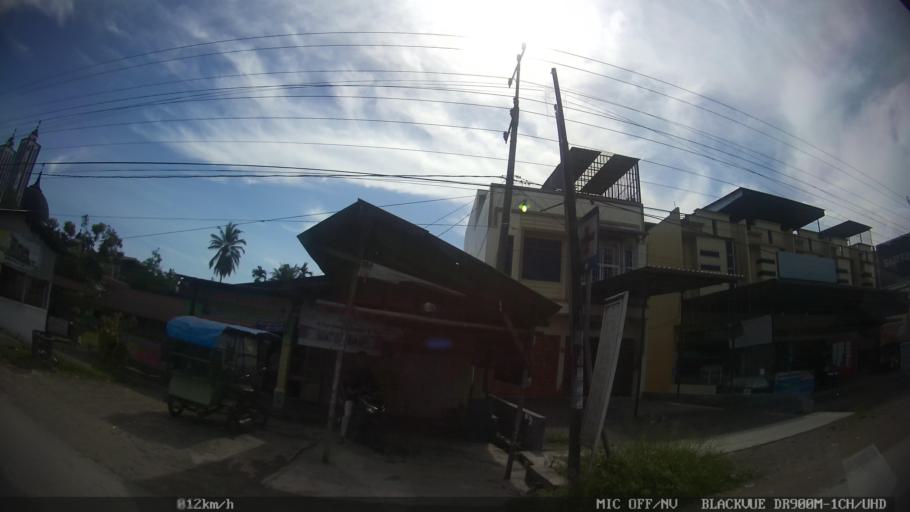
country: ID
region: North Sumatra
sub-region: Kabupaten Langkat
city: Stabat
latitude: 3.6865
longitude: 98.5089
